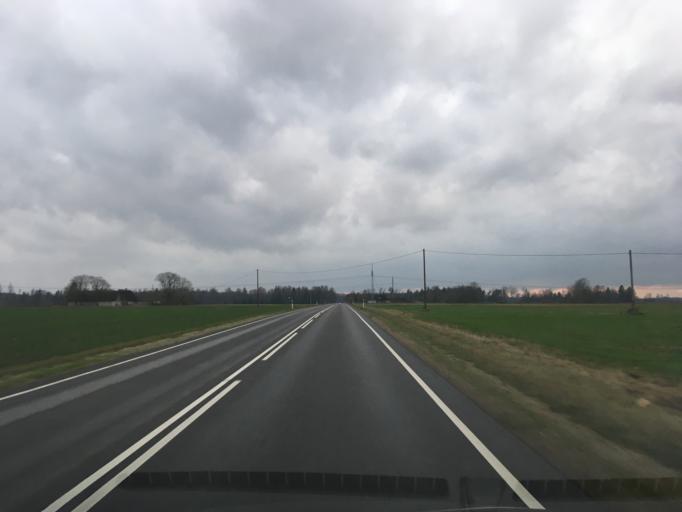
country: EE
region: Harju
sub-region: Anija vald
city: Kehra
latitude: 59.2524
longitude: 25.3182
